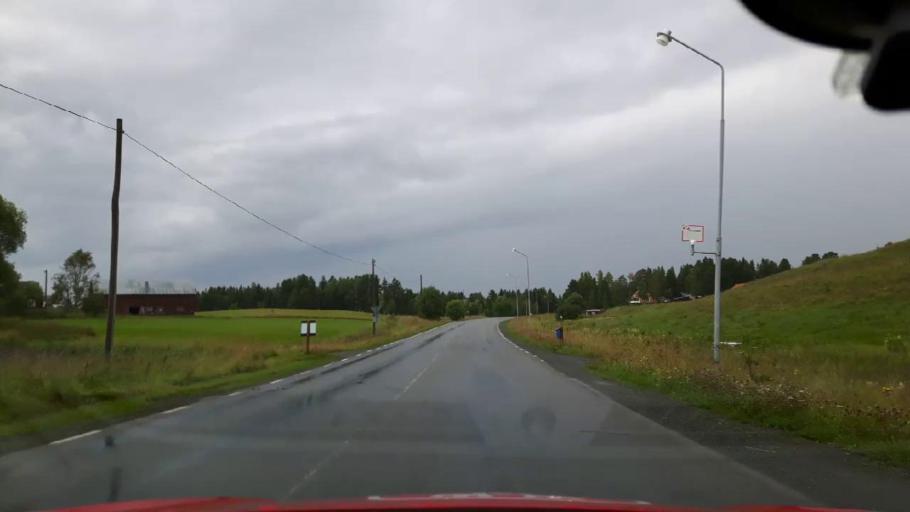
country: SE
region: Jaemtland
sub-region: Krokoms Kommun
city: Krokom
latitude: 63.3255
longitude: 14.2962
